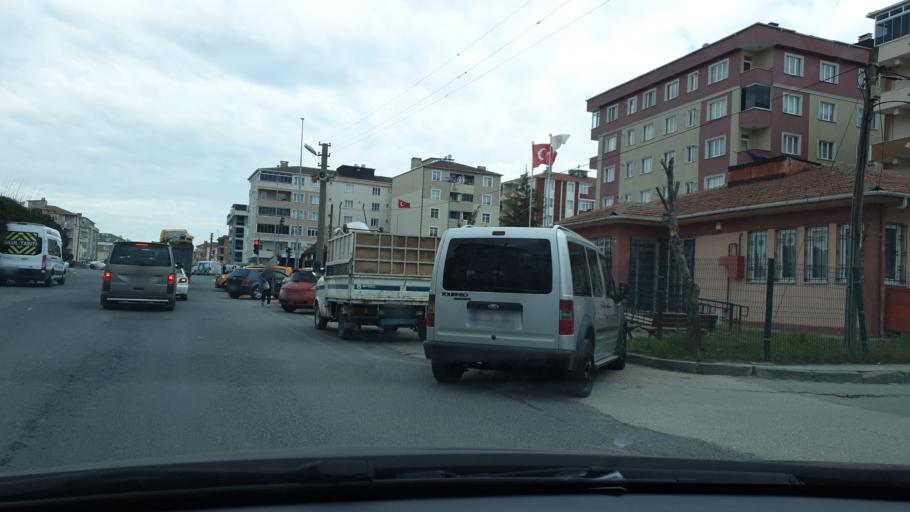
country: TR
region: Tekirdag
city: Cerkezkoey
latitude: 41.2846
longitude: 27.9880
